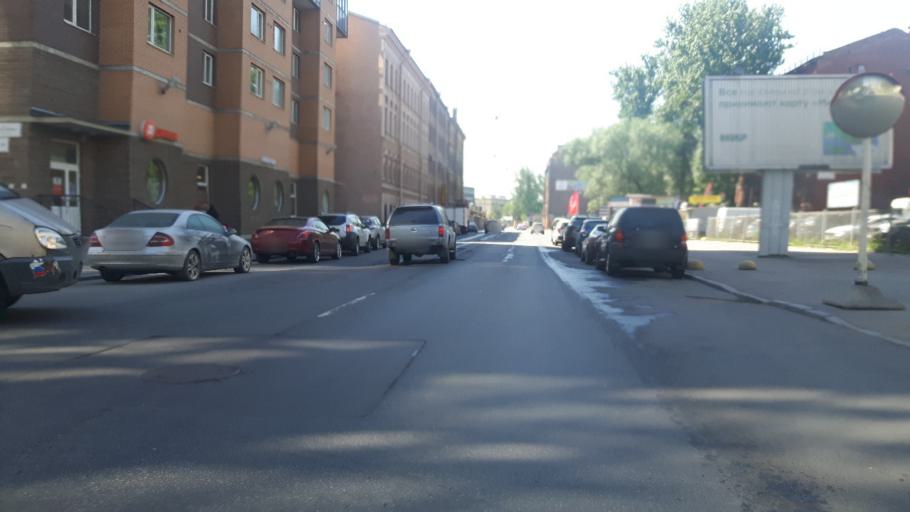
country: RU
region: St.-Petersburg
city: Admiralteisky
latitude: 59.9053
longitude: 30.2890
